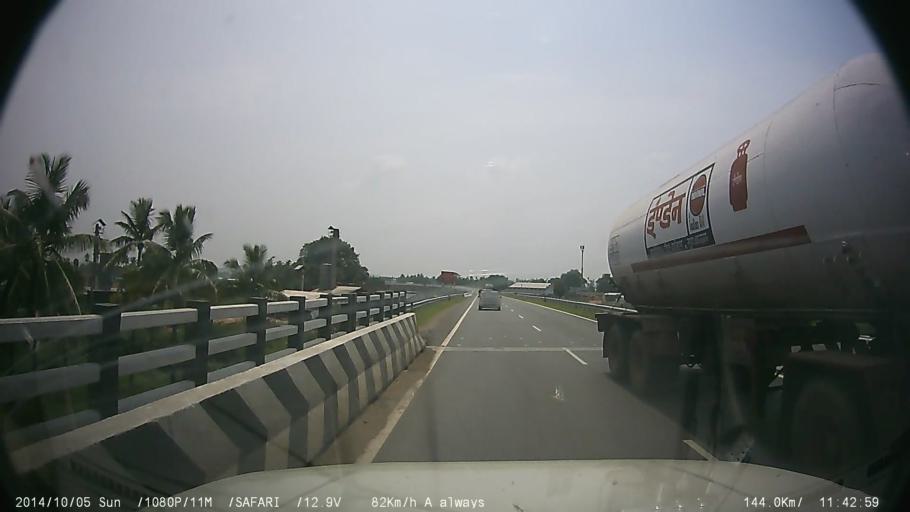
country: IN
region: Tamil Nadu
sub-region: Salem
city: Attur
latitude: 11.5972
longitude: 78.6185
